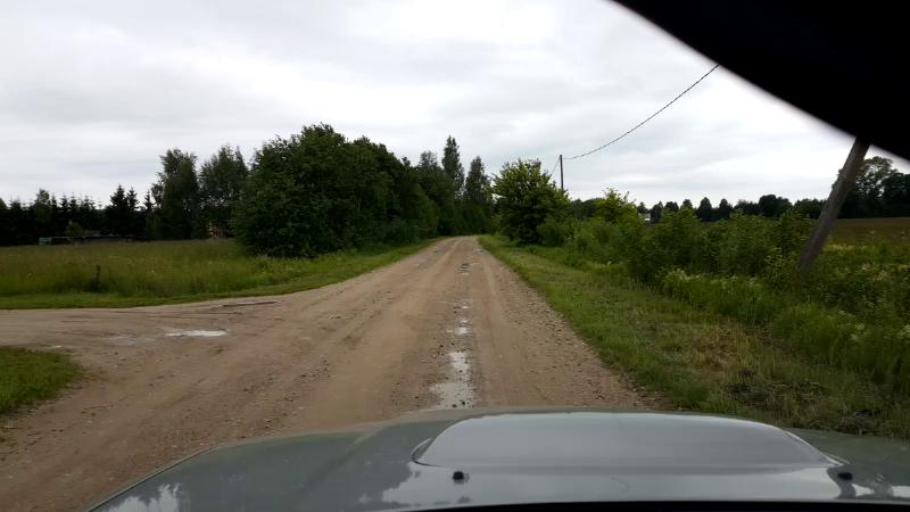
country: EE
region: Paernumaa
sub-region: Halinga vald
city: Parnu-Jaagupi
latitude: 58.5317
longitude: 24.5596
